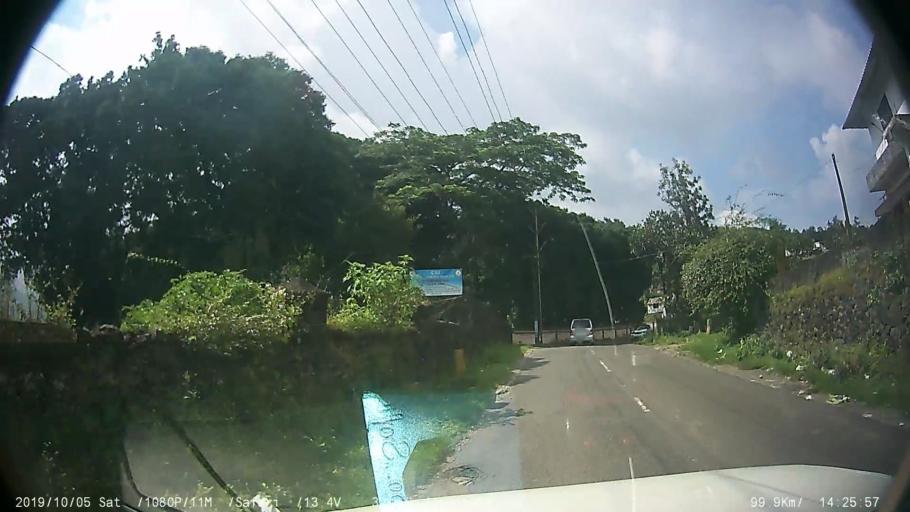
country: IN
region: Kerala
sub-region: Kottayam
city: Erattupetta
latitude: 9.5974
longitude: 76.9690
